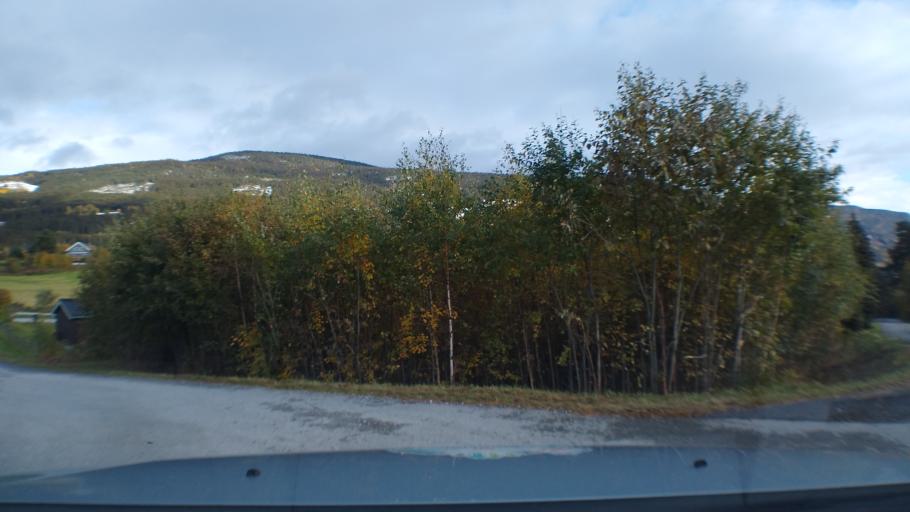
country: NO
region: Oppland
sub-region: Ringebu
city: Ringebu
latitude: 61.5348
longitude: 10.1335
